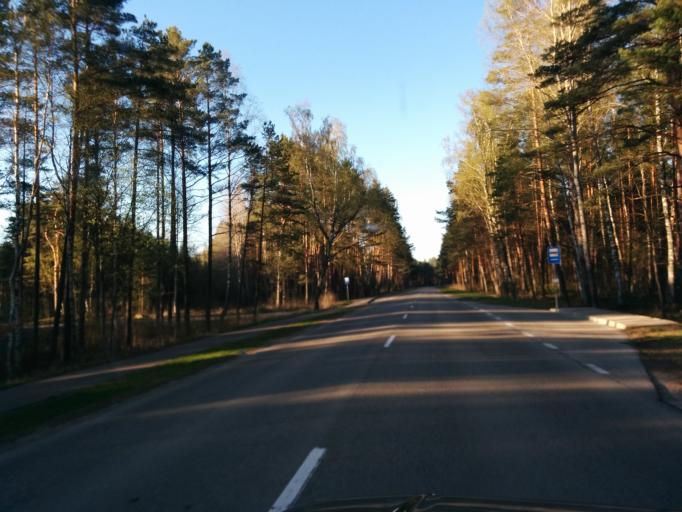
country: LV
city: Tireli
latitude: 56.9675
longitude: 23.5315
